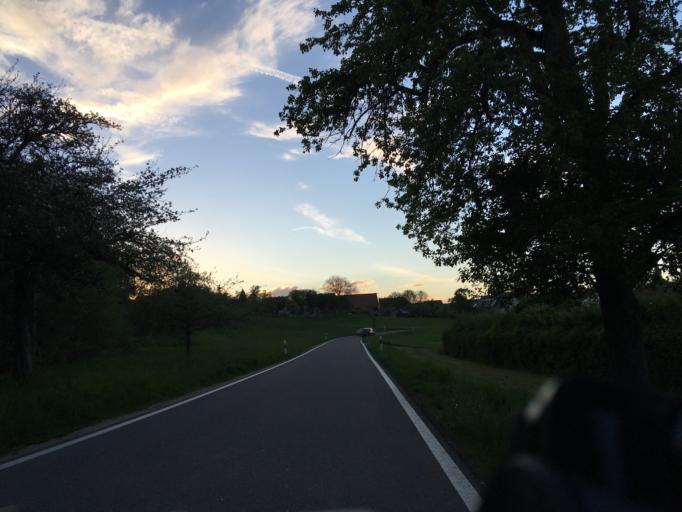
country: DE
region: Baden-Wuerttemberg
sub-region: Freiburg Region
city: Gailingen
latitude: 47.7195
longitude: 8.7579
